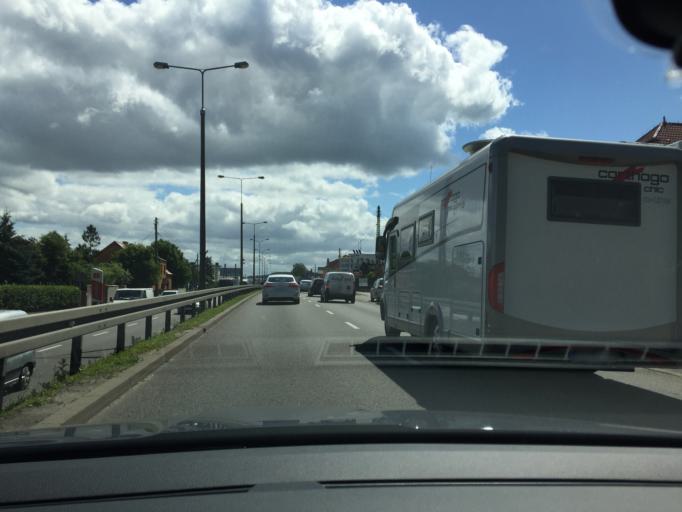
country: PL
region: Pomeranian Voivodeship
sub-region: Powiat wejherowski
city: Rumia
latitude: 54.5787
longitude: 18.3736
